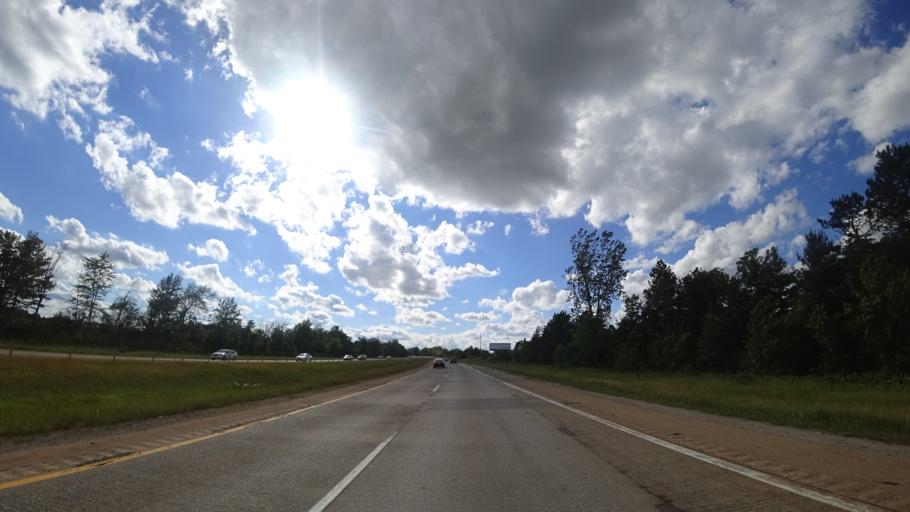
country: US
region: Michigan
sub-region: Ionia County
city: Portland
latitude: 42.8763
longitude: -84.9690
